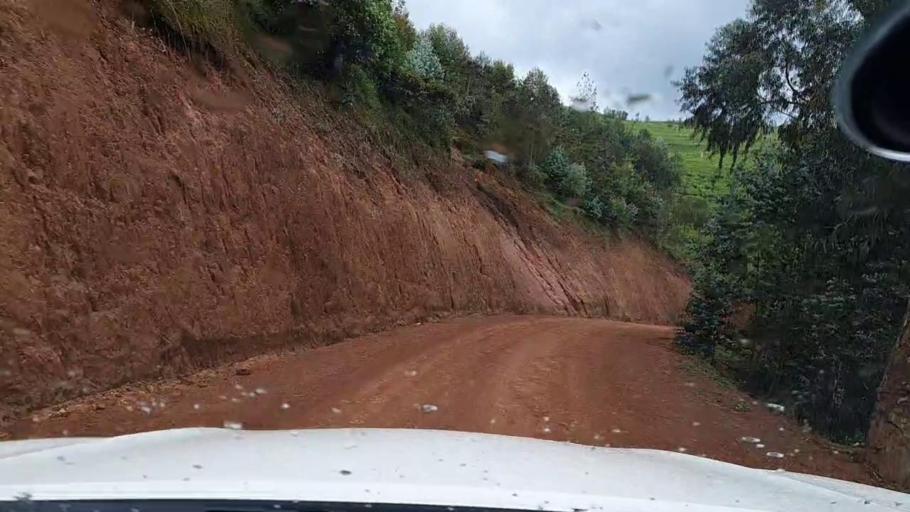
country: RW
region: Western Province
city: Kibuye
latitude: -2.1688
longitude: 29.4355
